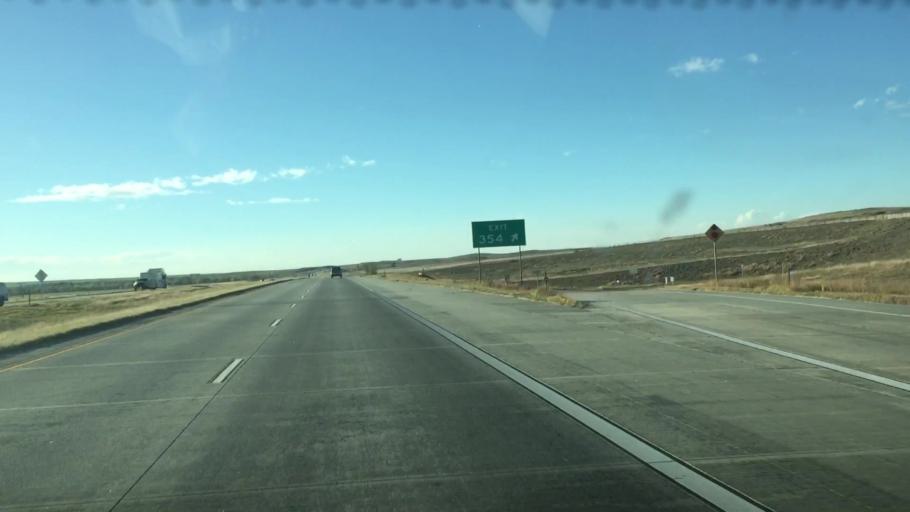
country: US
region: Colorado
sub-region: Lincoln County
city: Limon
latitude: 39.2904
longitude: -103.7935
